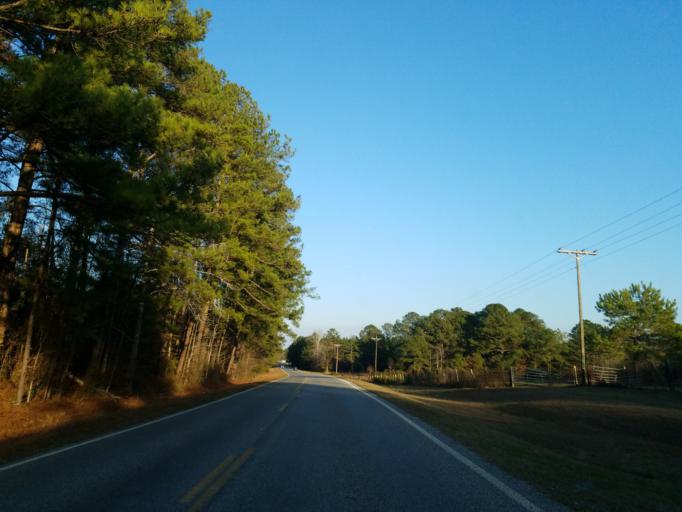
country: US
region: Mississippi
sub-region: Clarke County
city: Stonewall
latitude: 32.1679
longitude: -88.8473
